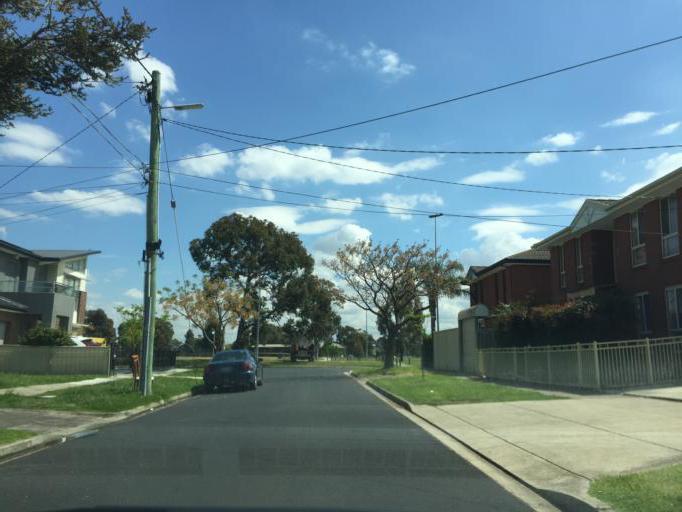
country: AU
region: Victoria
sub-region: Maribyrnong
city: Maidstone
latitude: -37.7881
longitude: 144.8690
